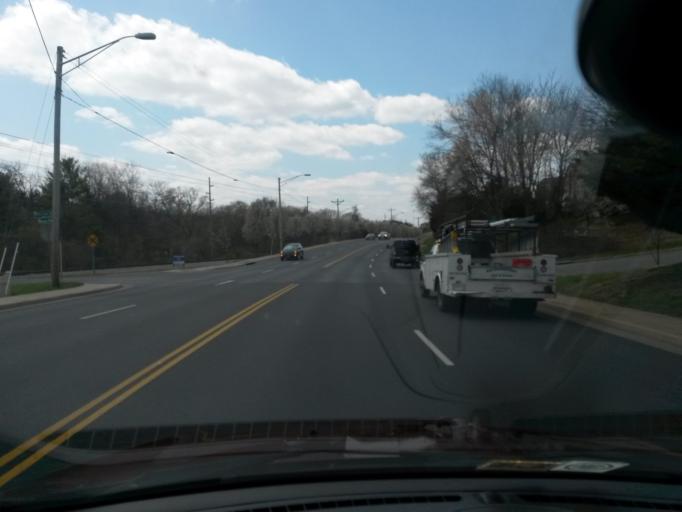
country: US
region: Virginia
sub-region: City of Harrisonburg
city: Harrisonburg
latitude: 38.4399
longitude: -78.8589
